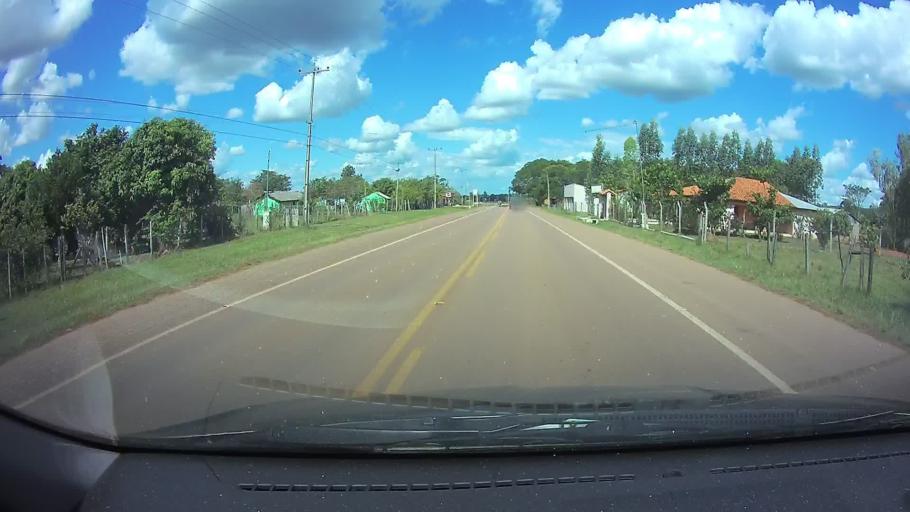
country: PY
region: Guaira
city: Itape
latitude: -25.9166
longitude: -56.6912
